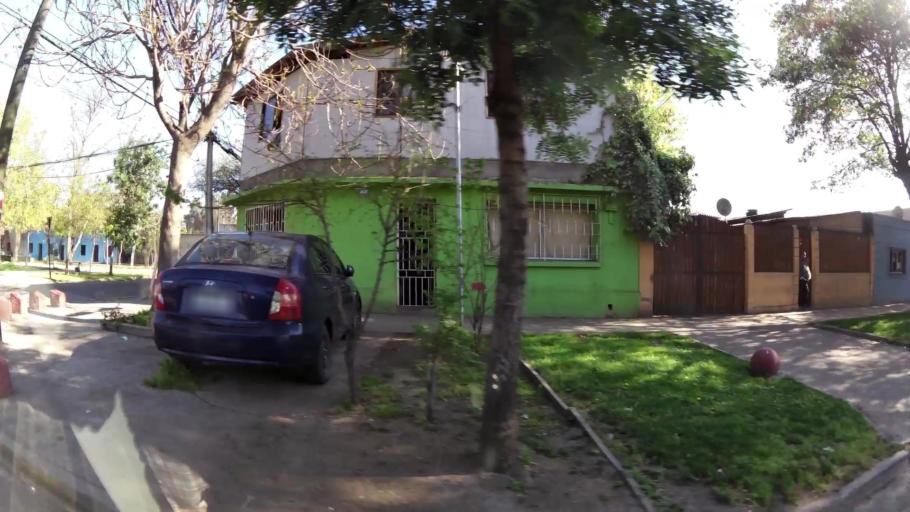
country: CL
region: Santiago Metropolitan
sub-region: Provincia de Santiago
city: Lo Prado
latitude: -33.4002
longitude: -70.6790
